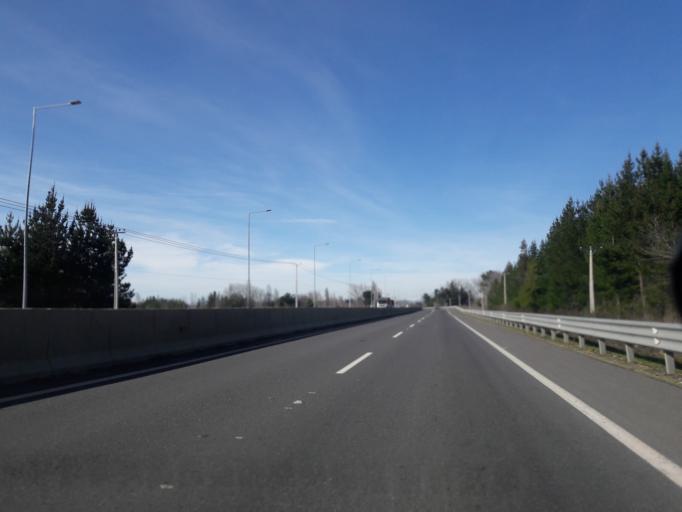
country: CL
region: Biobio
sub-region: Provincia de Biobio
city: Cabrero
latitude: -37.0216
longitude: -72.4715
